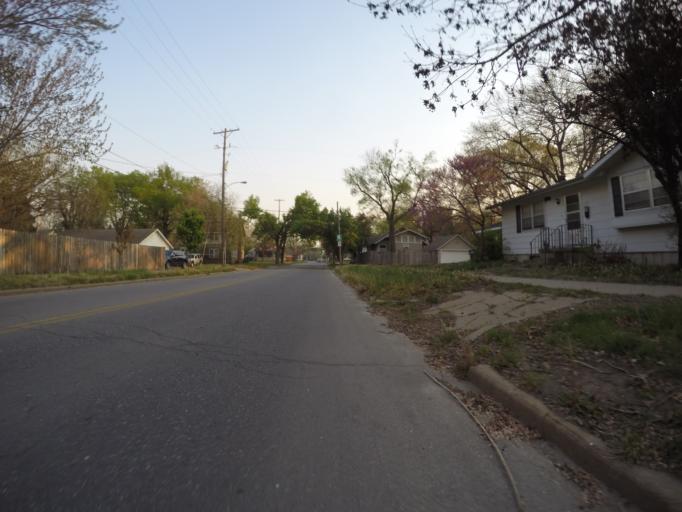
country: US
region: Kansas
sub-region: Riley County
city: Manhattan
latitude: 39.1814
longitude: -96.5833
